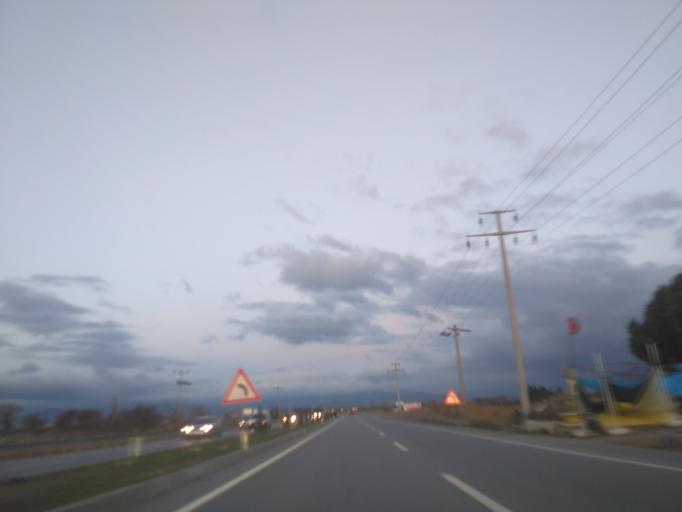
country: TR
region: Balikesir
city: Burhaniye
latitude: 39.5231
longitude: 26.9989
